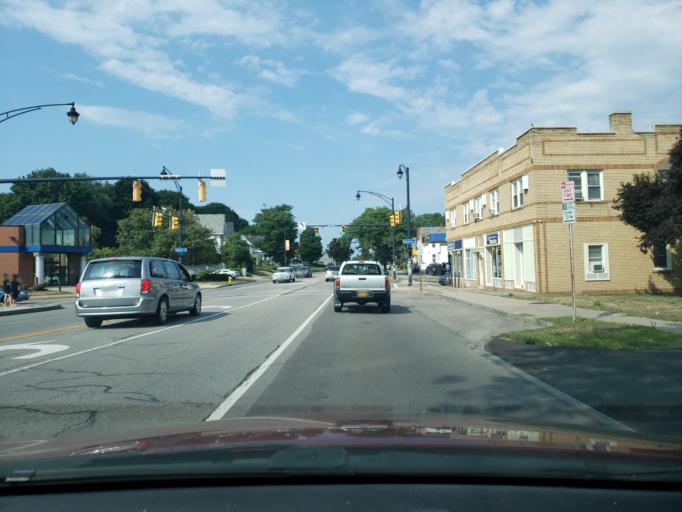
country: US
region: New York
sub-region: Monroe County
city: Irondequoit
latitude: 43.2413
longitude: -77.6205
